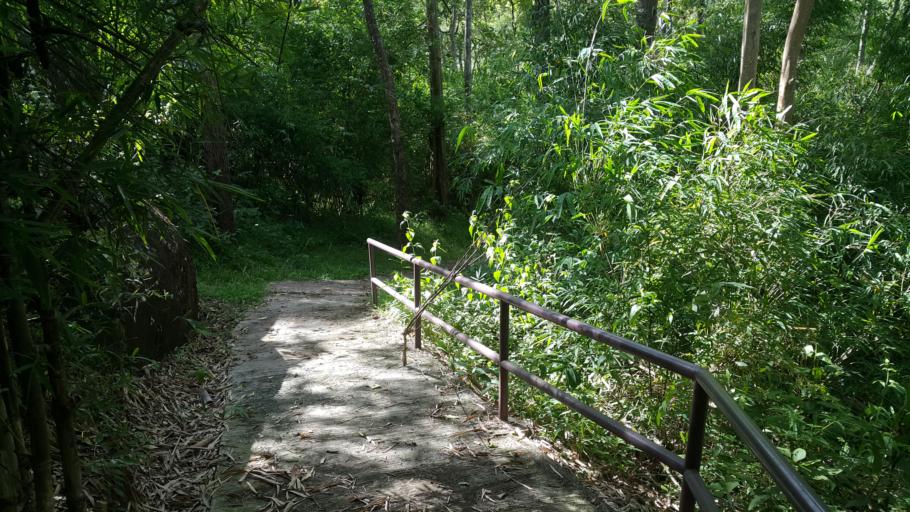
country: TH
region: Loei
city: Na Haeo
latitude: 17.5649
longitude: 100.9919
